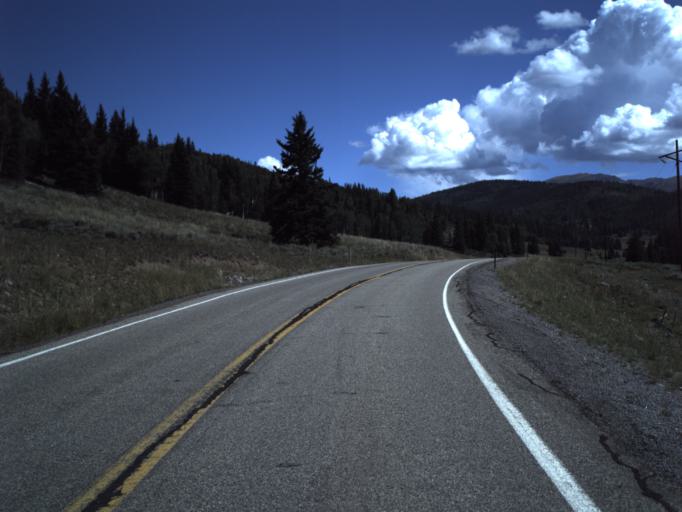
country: US
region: Utah
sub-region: Beaver County
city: Beaver
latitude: 38.2896
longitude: -112.4445
